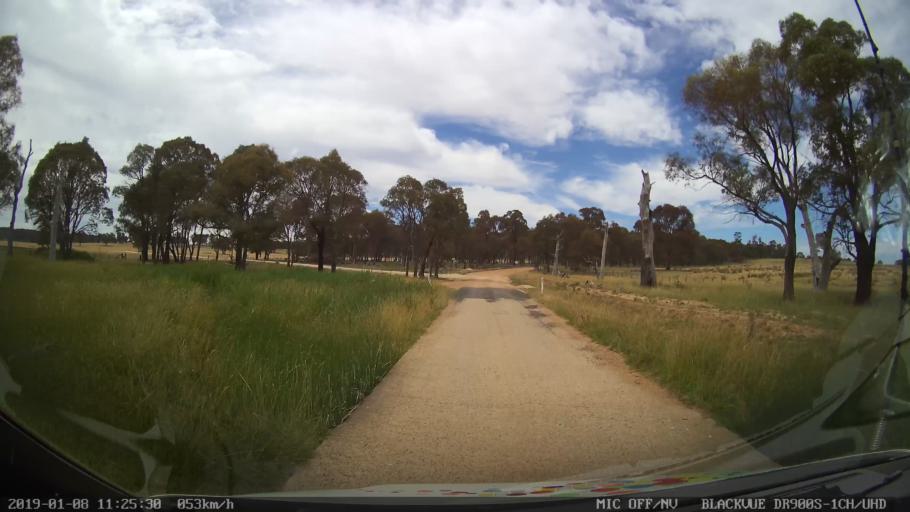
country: AU
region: New South Wales
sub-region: Guyra
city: Guyra
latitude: -30.2740
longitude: 151.5611
